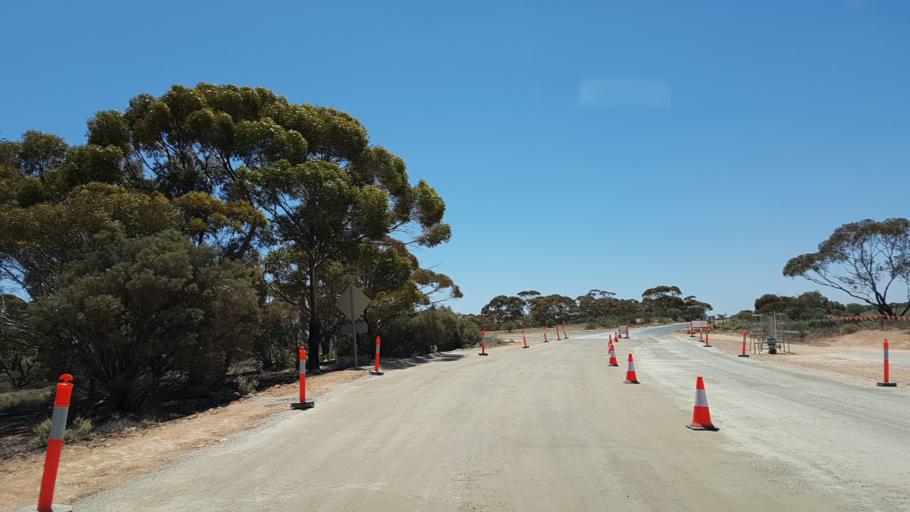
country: AU
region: South Australia
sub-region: Loxton Waikerie
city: Waikerie
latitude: -34.1875
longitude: 140.0176
